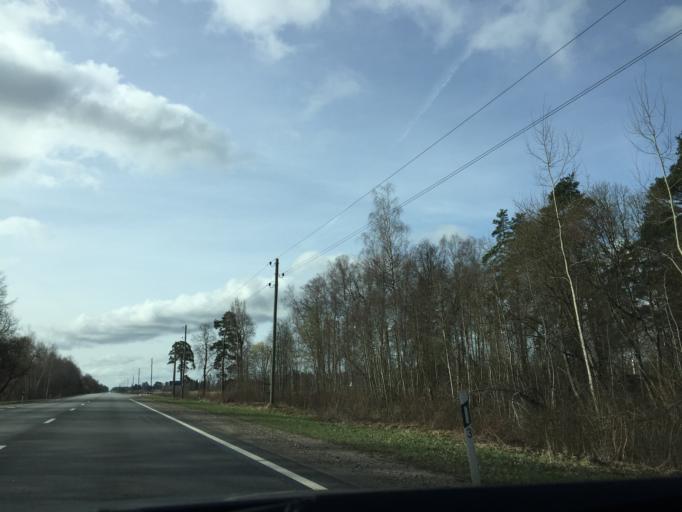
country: LV
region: Jelgava
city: Jelgava
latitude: 56.6048
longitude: 23.7207
